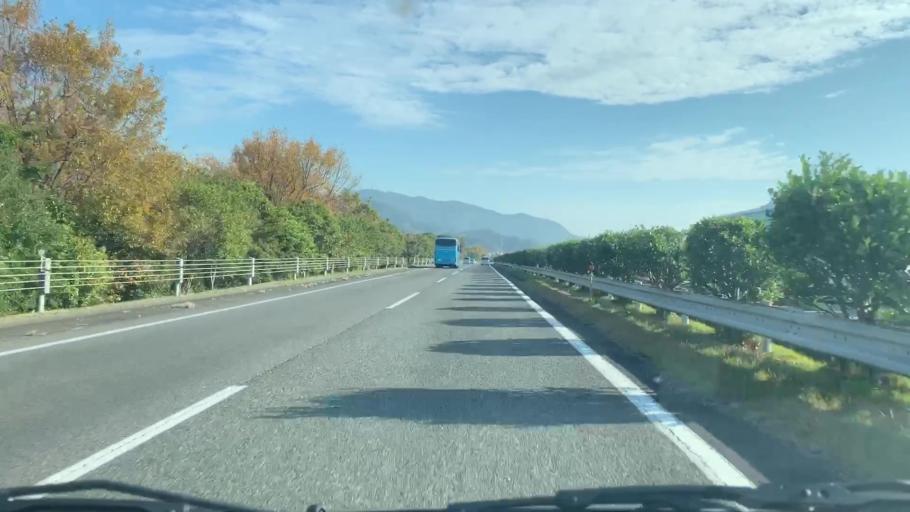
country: JP
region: Saga Prefecture
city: Saga-shi
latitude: 33.3127
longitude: 130.2527
